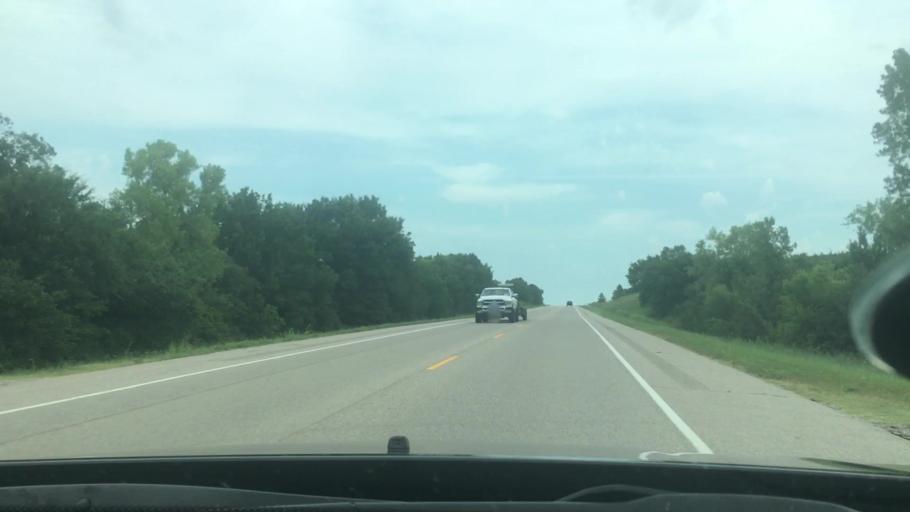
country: US
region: Oklahoma
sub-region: Seminole County
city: Konawa
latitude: 35.0100
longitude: -96.6786
